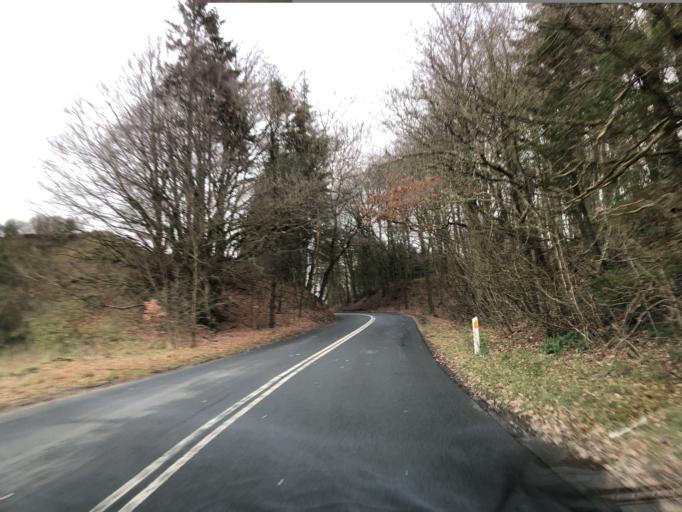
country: DK
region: Central Jutland
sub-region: Viborg Kommune
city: Stoholm
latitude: 56.4614
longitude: 9.1400
